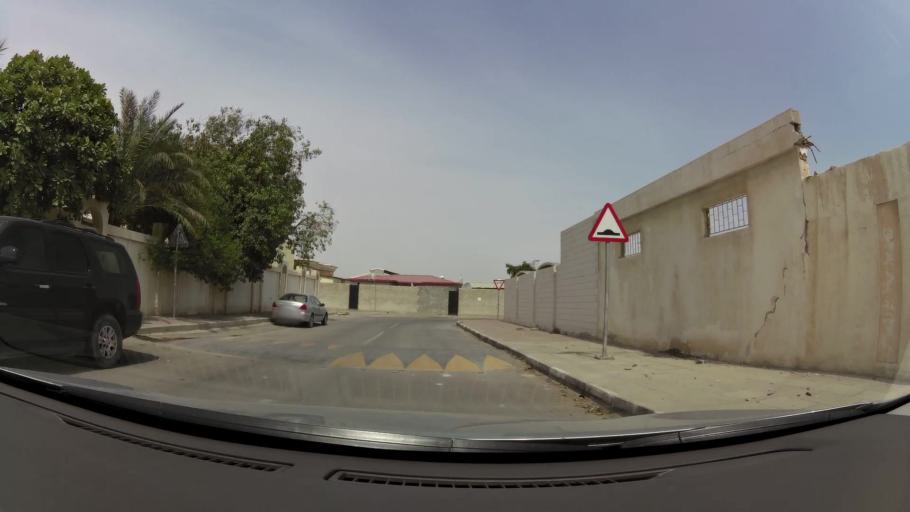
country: QA
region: Baladiyat ad Dawhah
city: Doha
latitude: 25.2704
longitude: 51.4916
